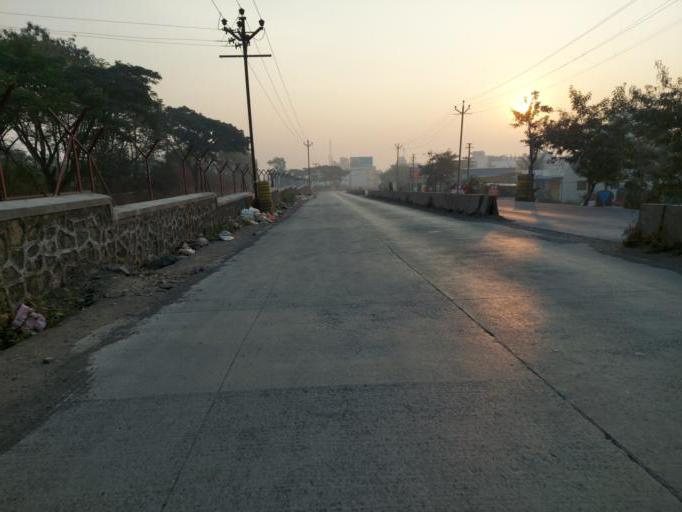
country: IN
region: Maharashtra
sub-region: Pune Division
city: Pune
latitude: 18.4663
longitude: 73.9579
